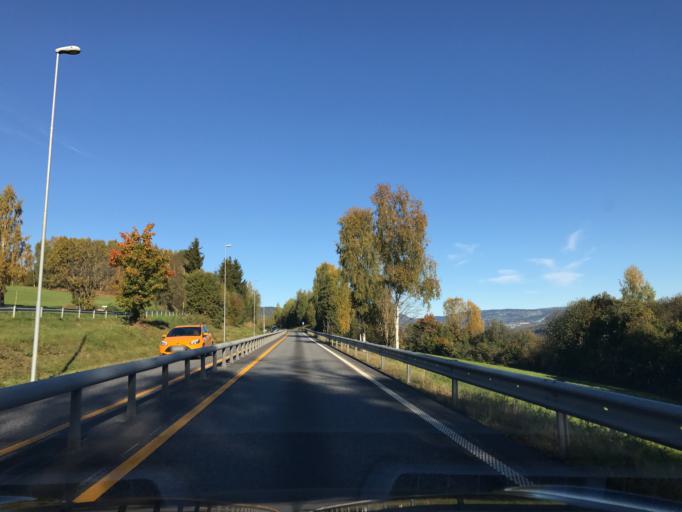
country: NO
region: Oppland
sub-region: Lillehammer
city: Lillehammer
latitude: 61.0363
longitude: 10.4405
